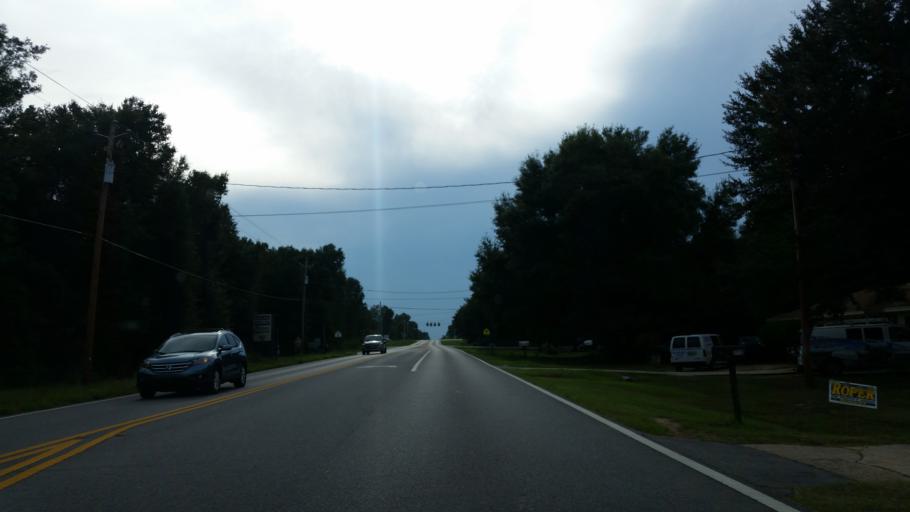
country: US
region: Florida
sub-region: Santa Rosa County
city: Bagdad
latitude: 30.5739
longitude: -87.0945
